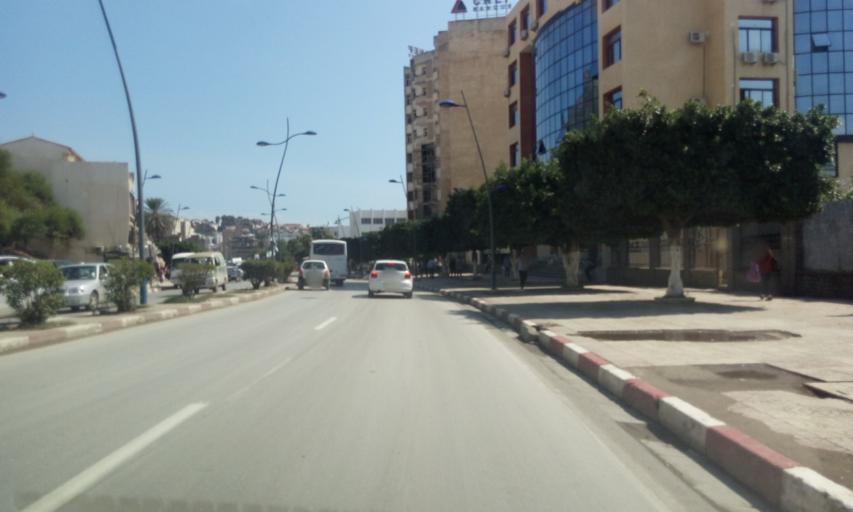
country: DZ
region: Bejaia
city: Bejaia
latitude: 36.7512
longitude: 5.0651
